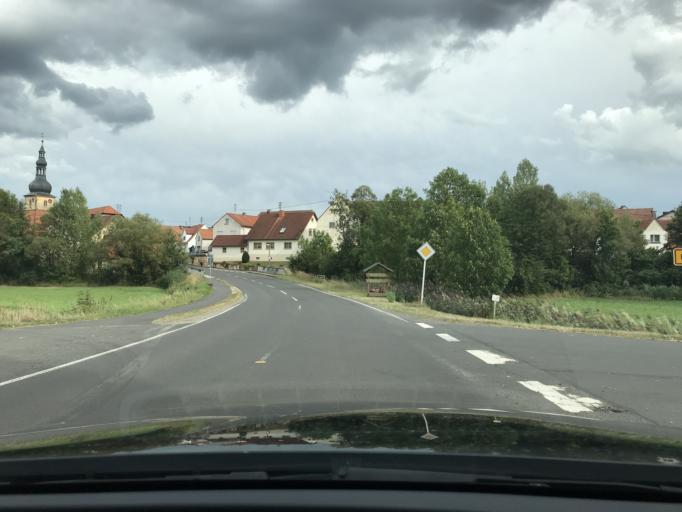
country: DE
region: Bavaria
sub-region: Regierungsbezirk Unterfranken
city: Hofheim in Unterfranken
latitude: 50.1235
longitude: 10.5300
